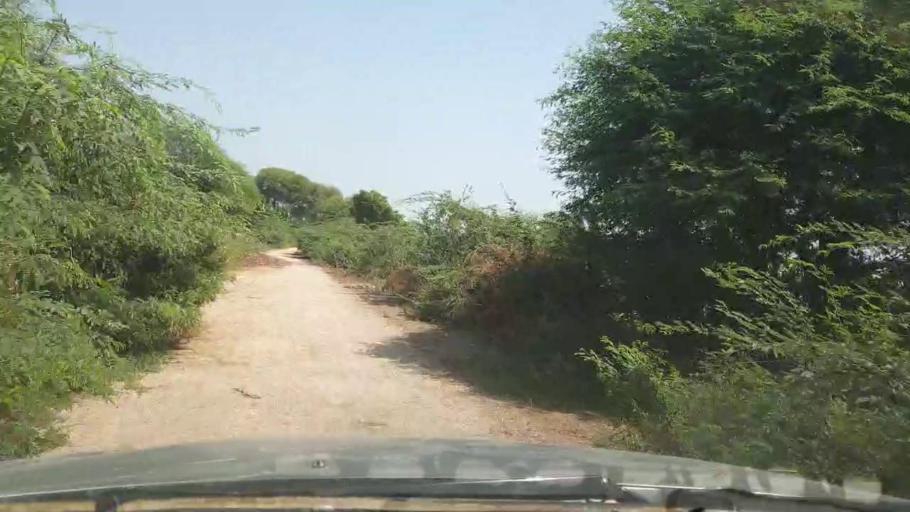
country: PK
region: Sindh
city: Tando Ghulam Ali
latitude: 25.1458
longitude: 68.8876
